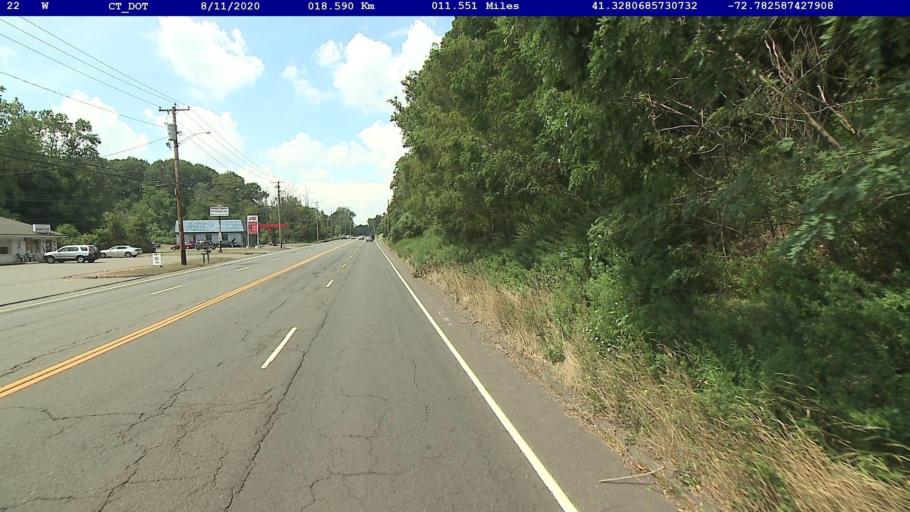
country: US
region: Connecticut
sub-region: New Haven County
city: North Branford
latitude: 41.3280
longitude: -72.7825
